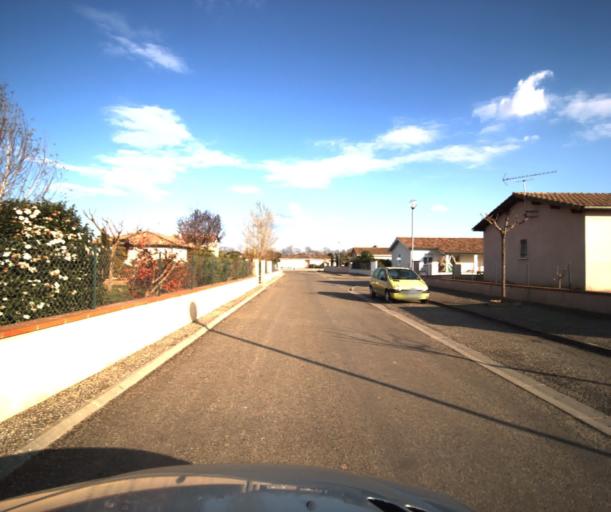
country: FR
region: Midi-Pyrenees
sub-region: Departement du Tarn-et-Garonne
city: Bressols
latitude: 43.9636
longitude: 1.3272
